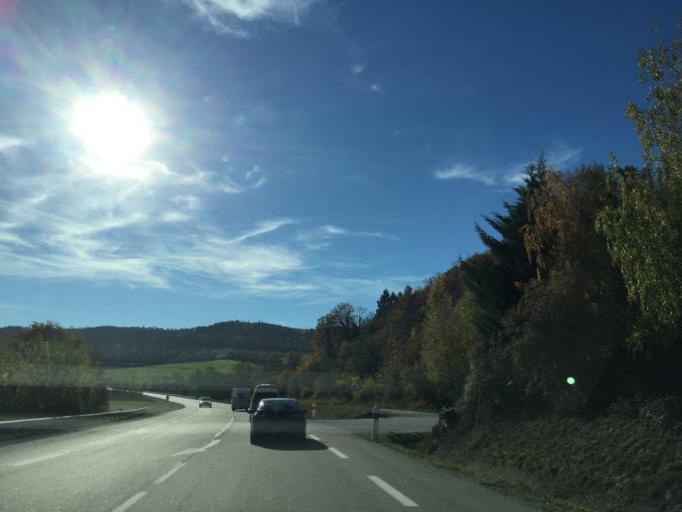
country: FR
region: Rhone-Alpes
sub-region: Departement de la Loire
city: Lentigny
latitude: 45.9316
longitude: 3.9757
